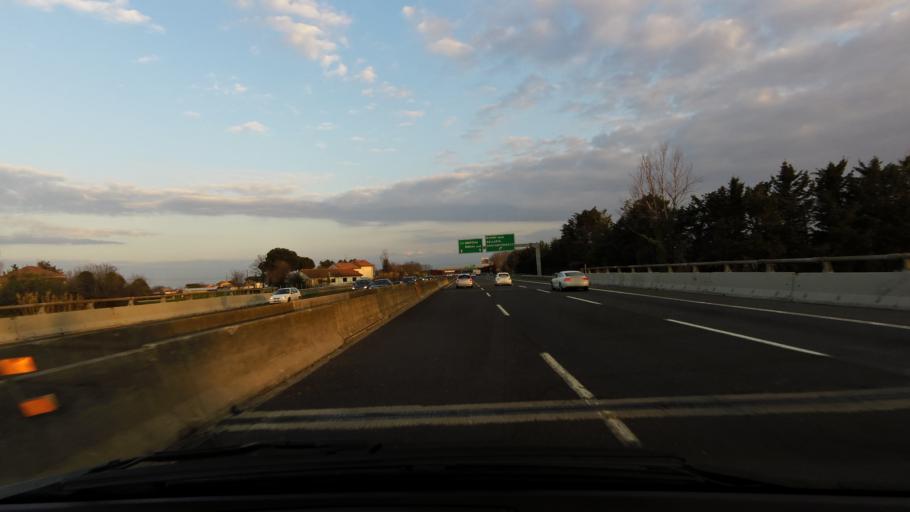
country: IT
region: Emilia-Romagna
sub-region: Provincia di Rimini
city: Santarcangelo
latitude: 44.0901
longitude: 12.4573
